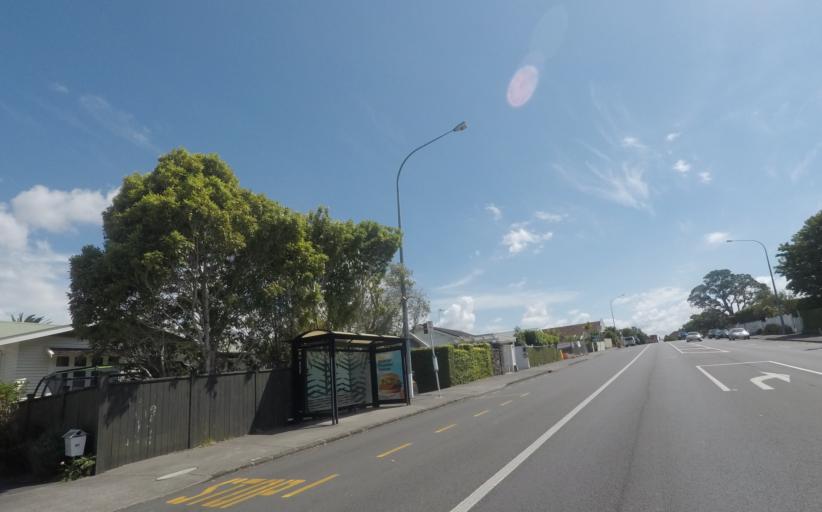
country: NZ
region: Auckland
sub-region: Auckland
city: Tamaki
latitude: -36.8798
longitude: 174.8172
